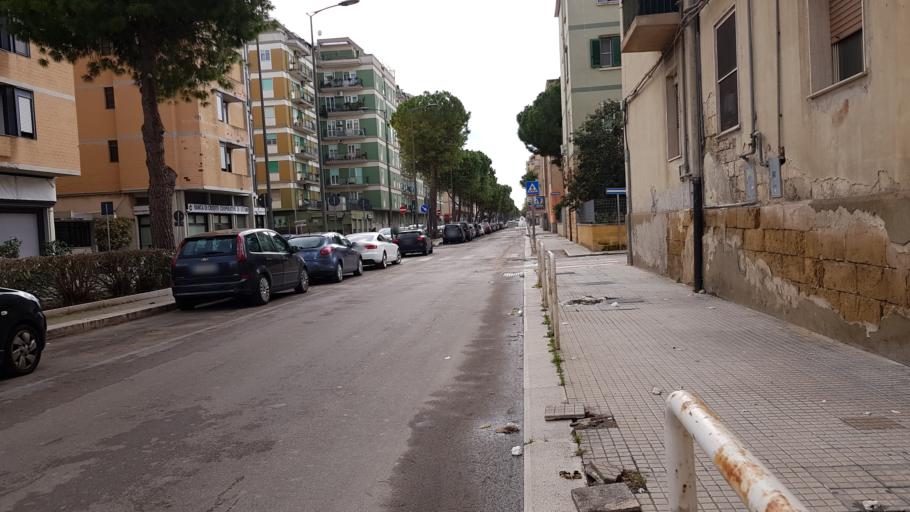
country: IT
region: Apulia
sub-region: Provincia di Brindisi
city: Brindisi
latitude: 40.6291
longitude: 17.9369
